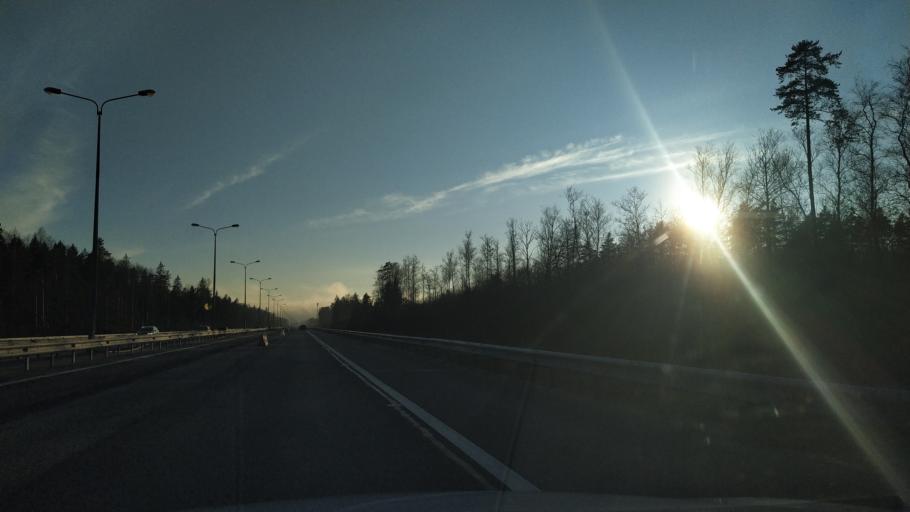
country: RU
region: St.-Petersburg
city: Ol'gino
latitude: 60.0513
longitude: 30.0877
